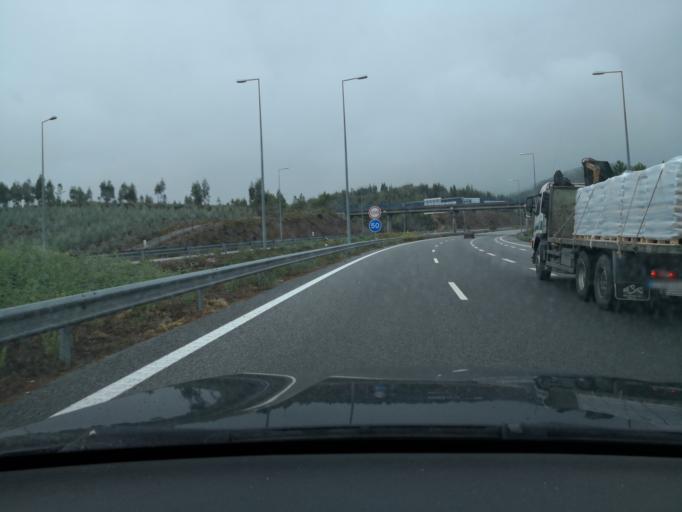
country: PT
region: Porto
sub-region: Valongo
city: Sobrado
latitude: 41.2330
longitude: -8.4528
